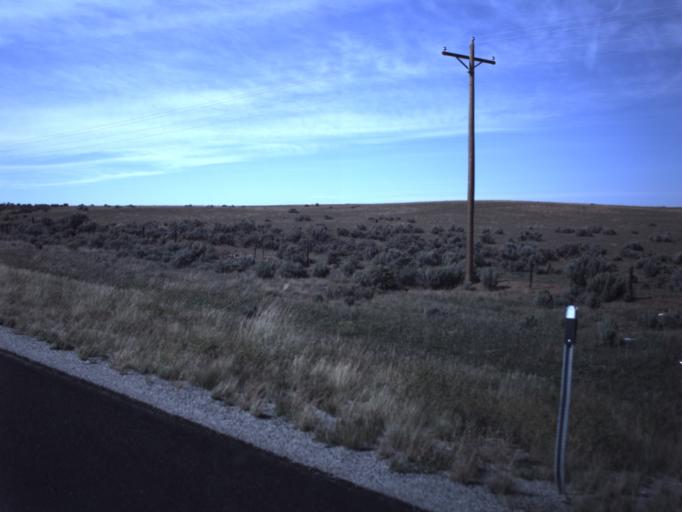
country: US
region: Utah
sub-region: San Juan County
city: Monticello
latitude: 37.8615
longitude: -109.2138
